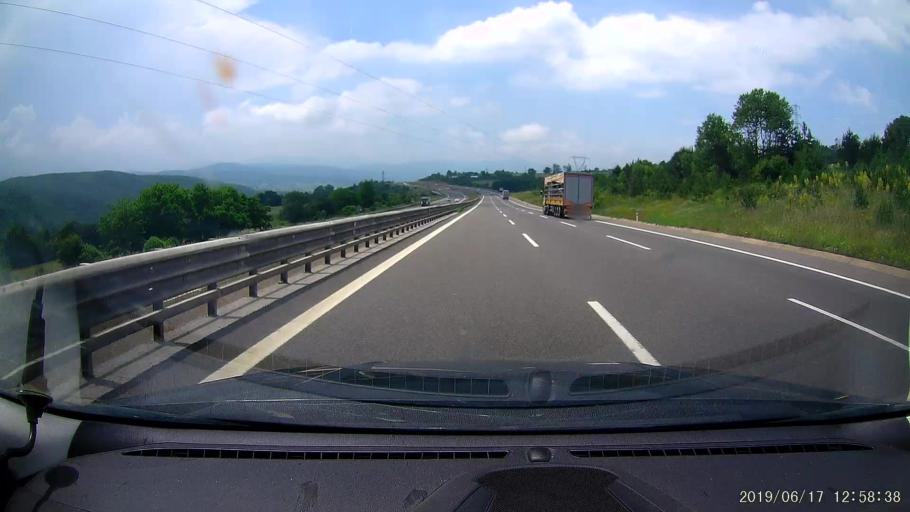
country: TR
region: Bolu
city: Bolu
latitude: 40.7308
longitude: 31.5178
